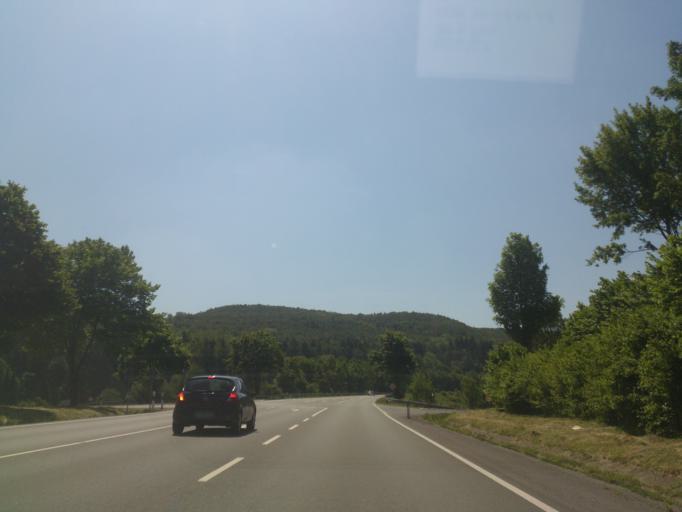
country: DE
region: North Rhine-Westphalia
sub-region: Regierungsbezirk Detmold
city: Bad Driburg
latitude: 51.7056
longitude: 9.0267
